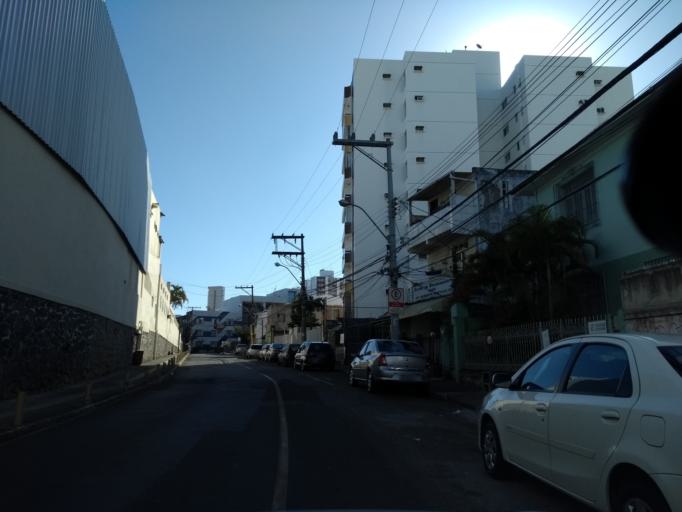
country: BR
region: Bahia
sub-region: Salvador
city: Salvador
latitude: -12.9915
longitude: -38.5149
